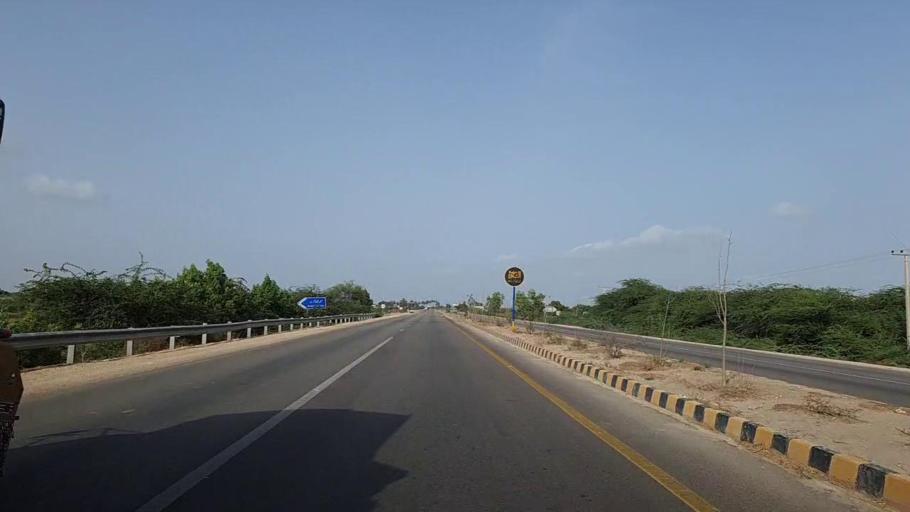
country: PK
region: Sindh
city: Gharo
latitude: 24.7335
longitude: 67.6948
